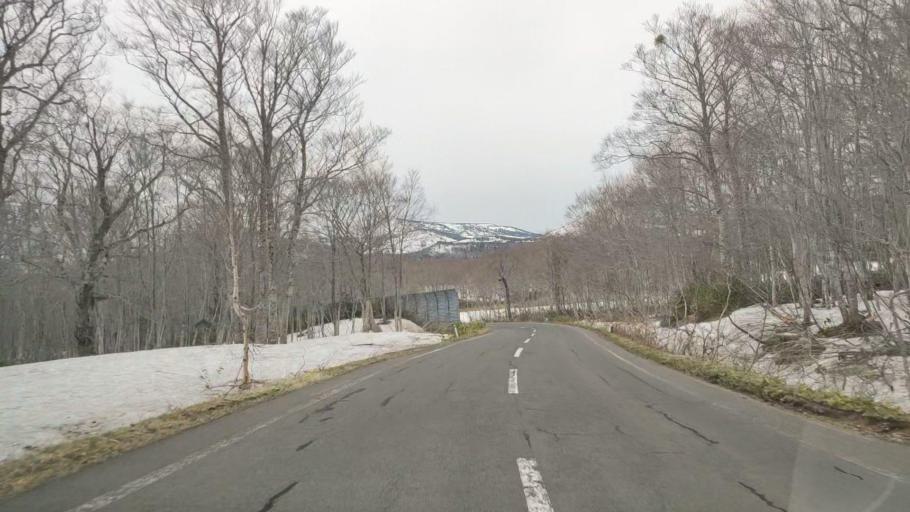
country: JP
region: Aomori
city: Aomori Shi
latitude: 40.6341
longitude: 140.9291
